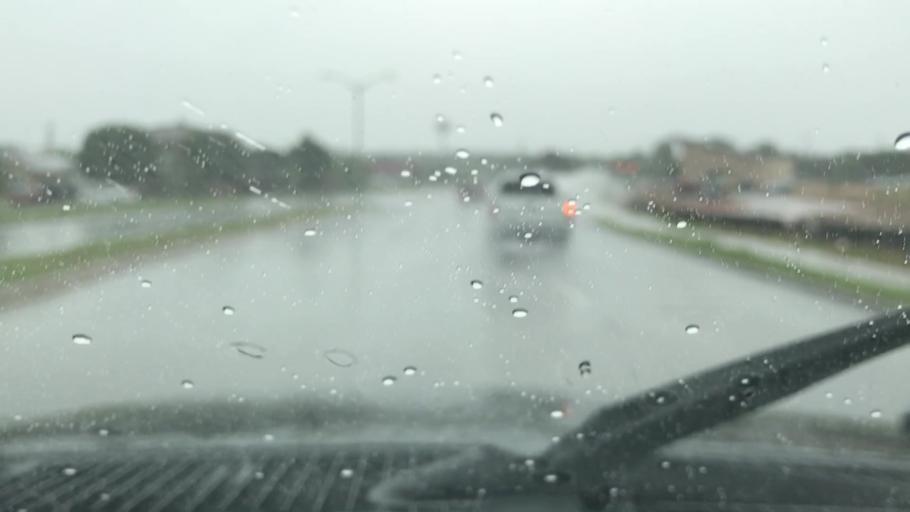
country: US
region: Texas
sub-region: Williamson County
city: Cedar Park
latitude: 30.5289
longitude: -97.8565
